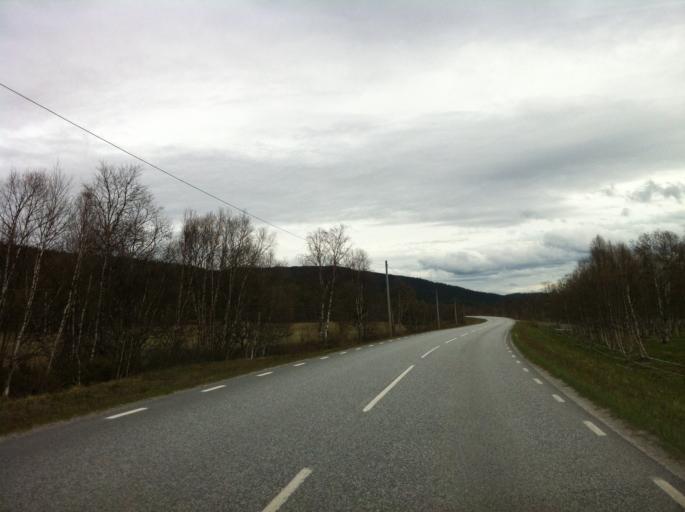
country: NO
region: Sor-Trondelag
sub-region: Tydal
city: Aas
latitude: 62.6209
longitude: 12.4725
